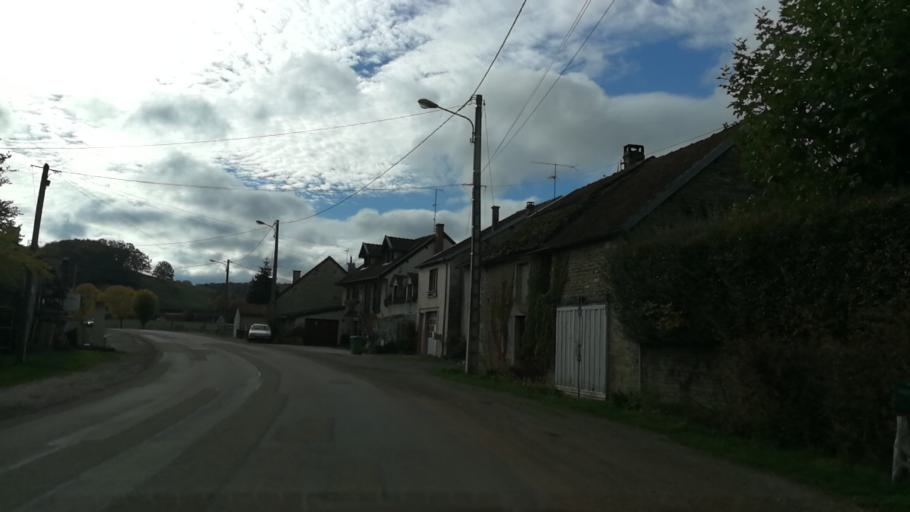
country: FR
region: Bourgogne
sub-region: Departement de la Cote-d'Or
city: Pouilly-en-Auxois
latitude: 47.2713
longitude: 4.4824
